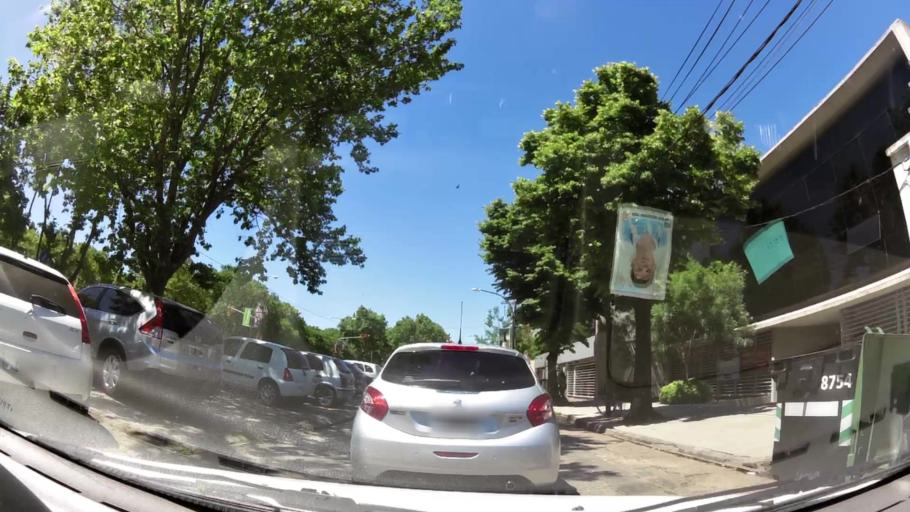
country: AR
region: Buenos Aires
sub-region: Partido de San Isidro
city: San Isidro
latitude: -34.4938
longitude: -58.5325
